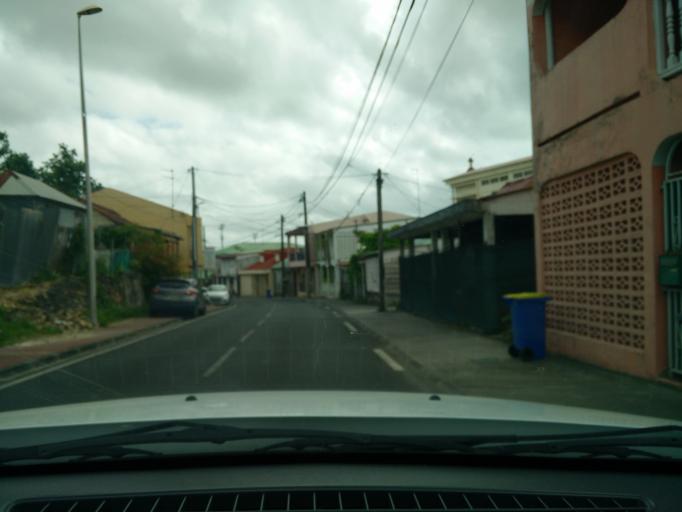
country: GP
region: Guadeloupe
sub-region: Guadeloupe
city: Petit-Canal
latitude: 16.3301
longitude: -61.4585
